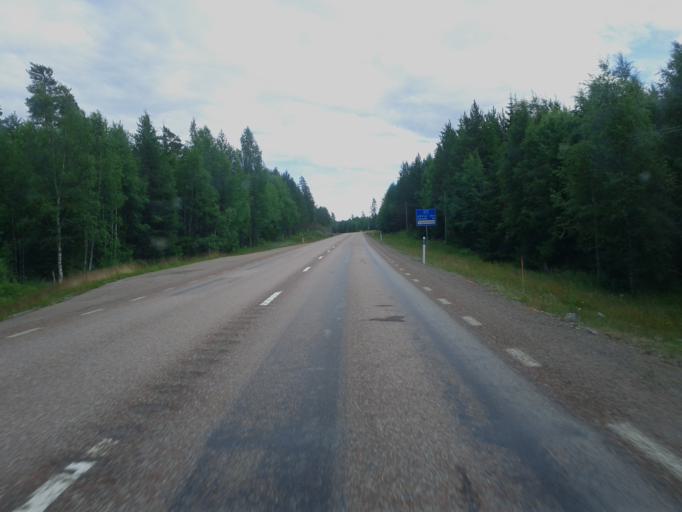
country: SE
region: Dalarna
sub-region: Faluns Kommun
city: Bjursas
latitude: 60.7919
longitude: 15.2781
